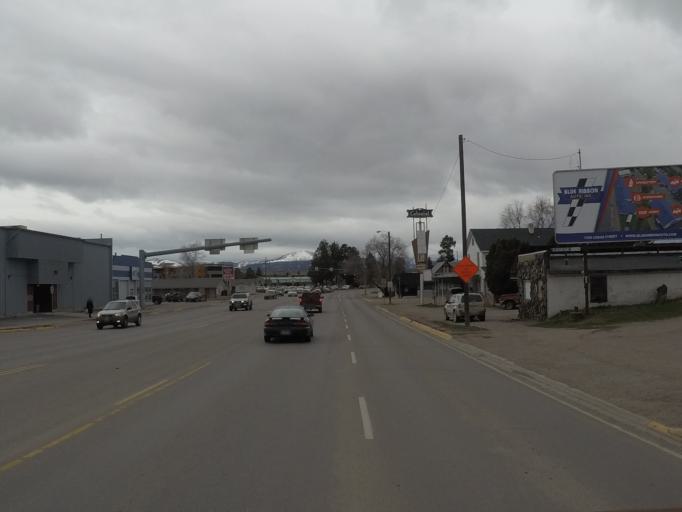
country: US
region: Montana
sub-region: Missoula County
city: Missoula
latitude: 46.8781
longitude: -114.0158
